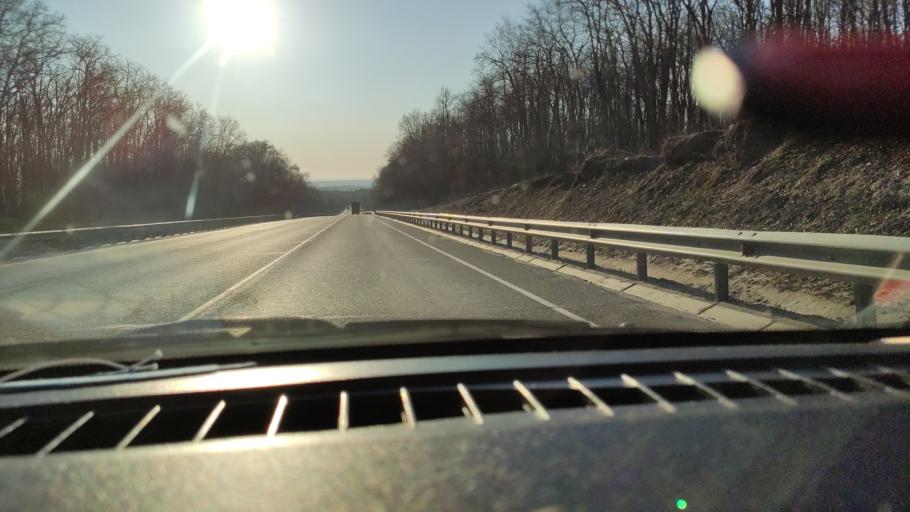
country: RU
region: Saratov
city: Vol'sk
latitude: 52.1072
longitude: 47.4135
